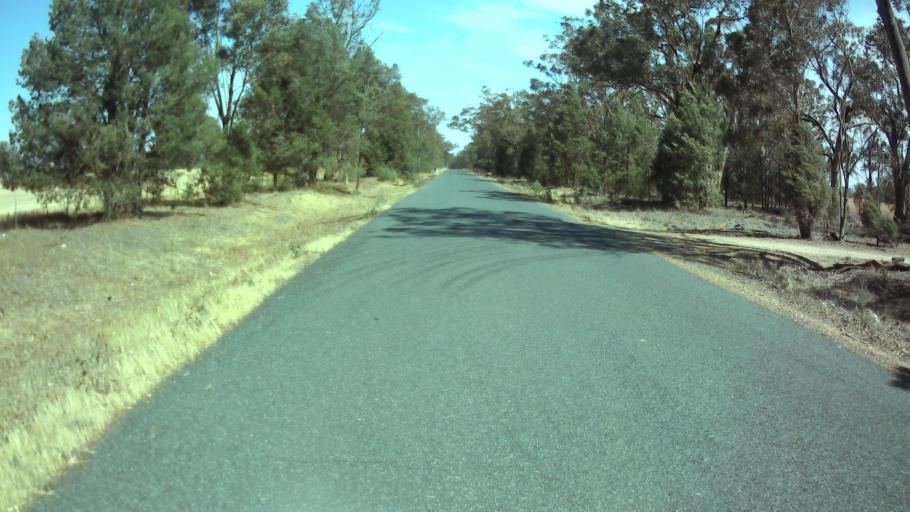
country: AU
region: New South Wales
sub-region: Weddin
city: Grenfell
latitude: -34.0614
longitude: 148.1333
